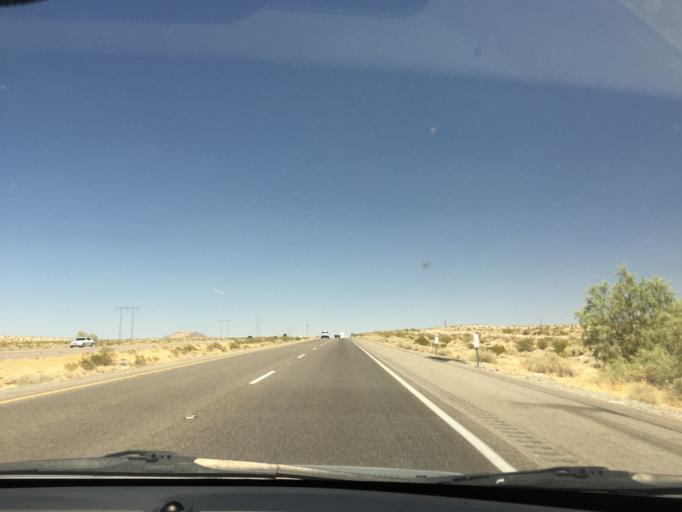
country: US
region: California
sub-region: San Bernardino County
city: Fort Irwin
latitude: 35.0073
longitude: -116.5410
